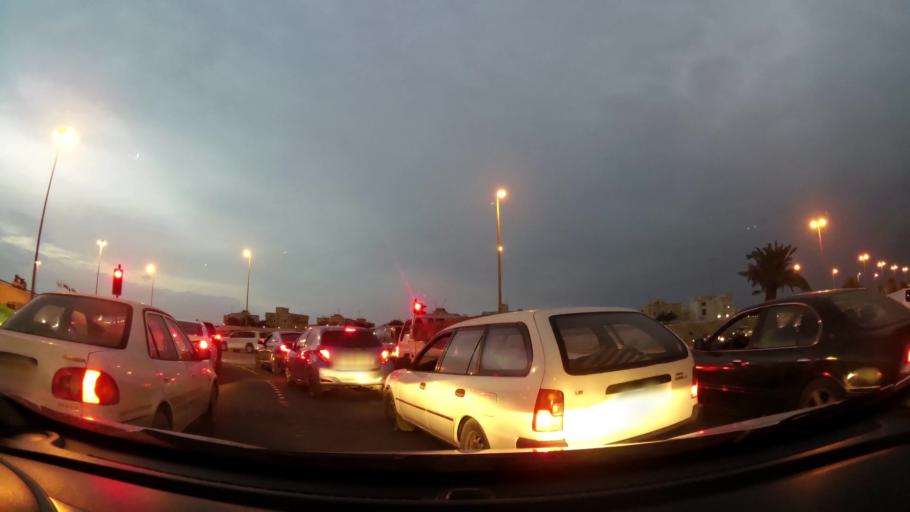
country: BH
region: Central Governorate
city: Madinat Hamad
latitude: 26.1395
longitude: 50.5113
